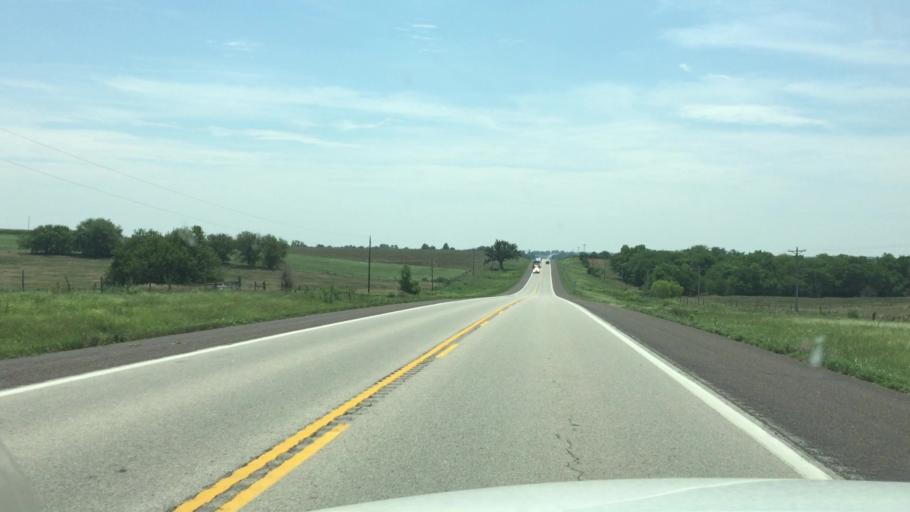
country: US
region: Kansas
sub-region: Jackson County
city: Holton
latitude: 39.6060
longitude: -95.7315
